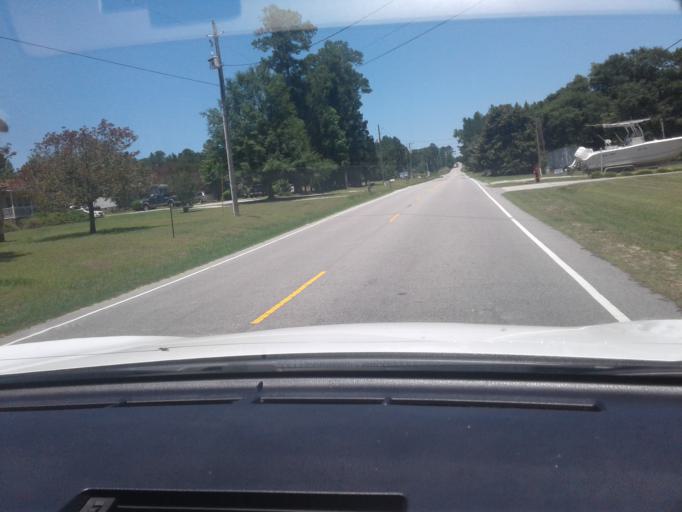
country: US
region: North Carolina
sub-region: Harnett County
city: Lillington
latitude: 35.3852
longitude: -78.8405
